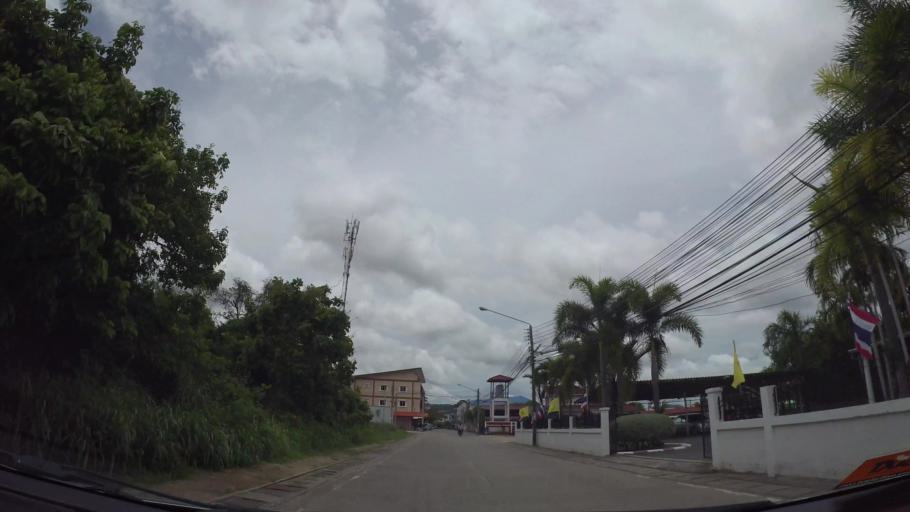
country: TH
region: Chon Buri
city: Sattahip
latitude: 12.7604
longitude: 100.9006
